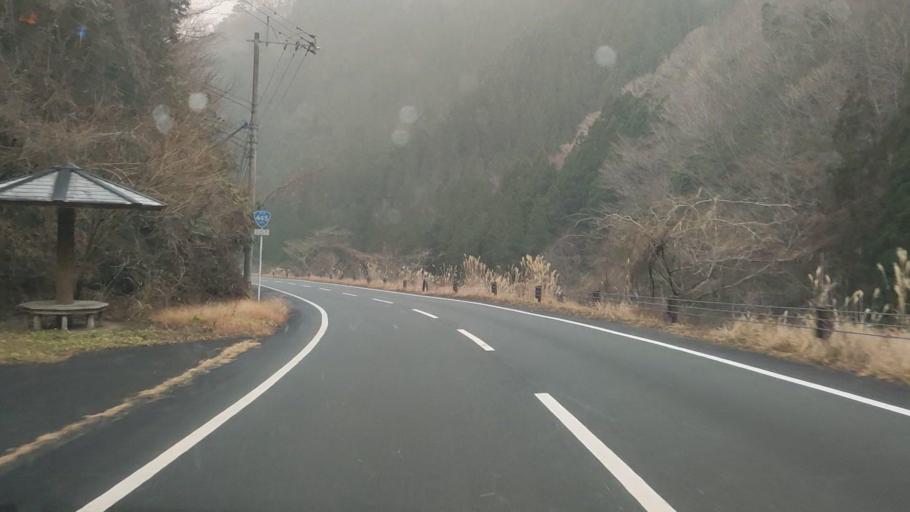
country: JP
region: Kumamoto
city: Matsubase
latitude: 32.5509
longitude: 130.9340
